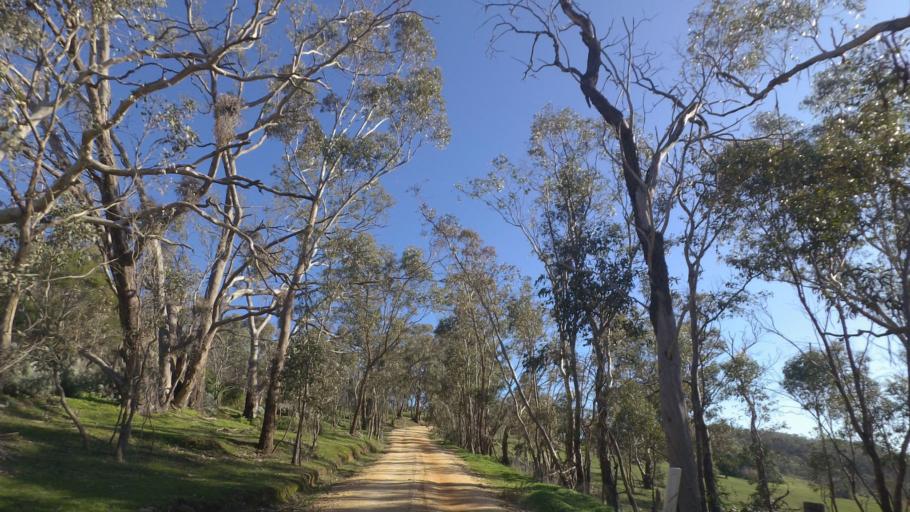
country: AU
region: Victoria
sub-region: Mount Alexander
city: Castlemaine
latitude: -37.0326
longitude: 144.2739
